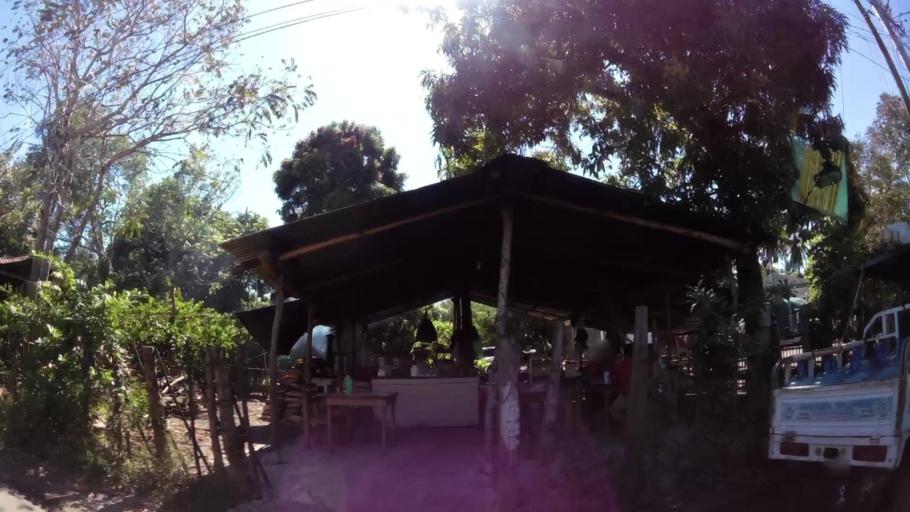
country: GT
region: Escuintla
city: Iztapa
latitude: 13.9396
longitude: -90.7096
